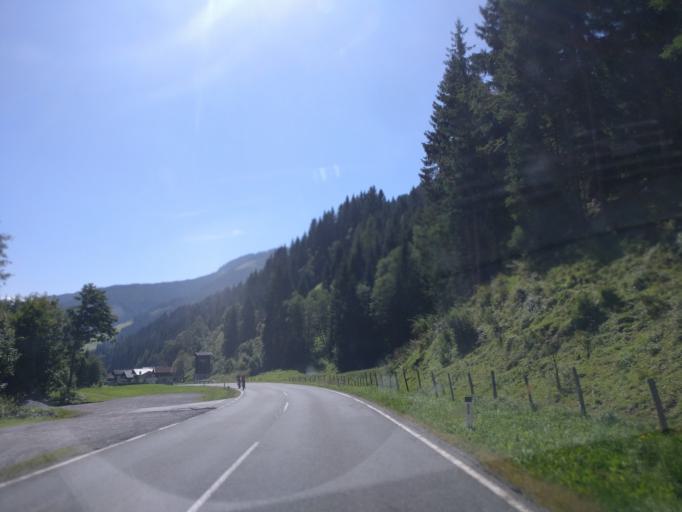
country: AT
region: Salzburg
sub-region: Politischer Bezirk Zell am See
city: Dienten am Hochkonig
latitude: 47.3693
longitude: 12.9975
